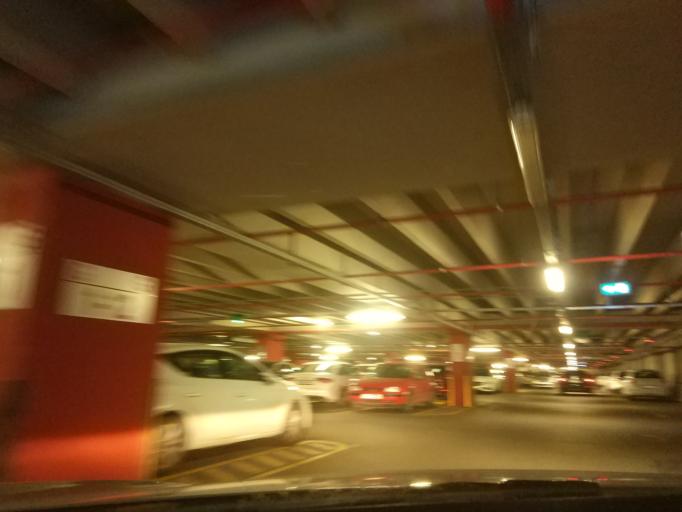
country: TR
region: Istanbul
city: Pendik
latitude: 40.9090
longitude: 29.3129
